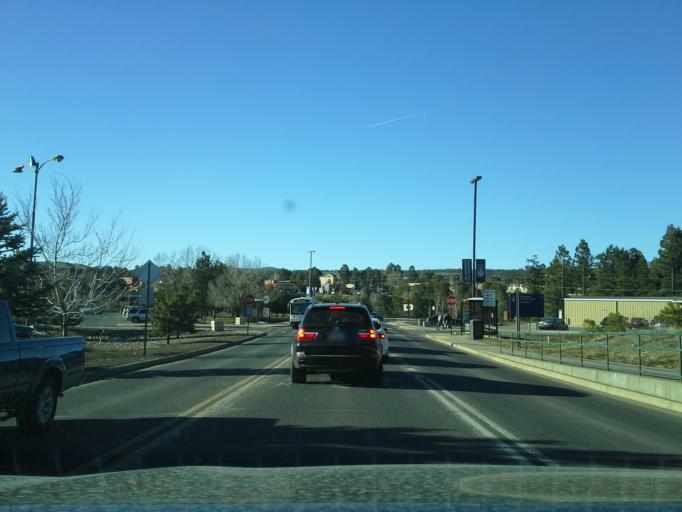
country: US
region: Arizona
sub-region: Coconino County
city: Flagstaff
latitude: 35.1763
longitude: -111.6590
